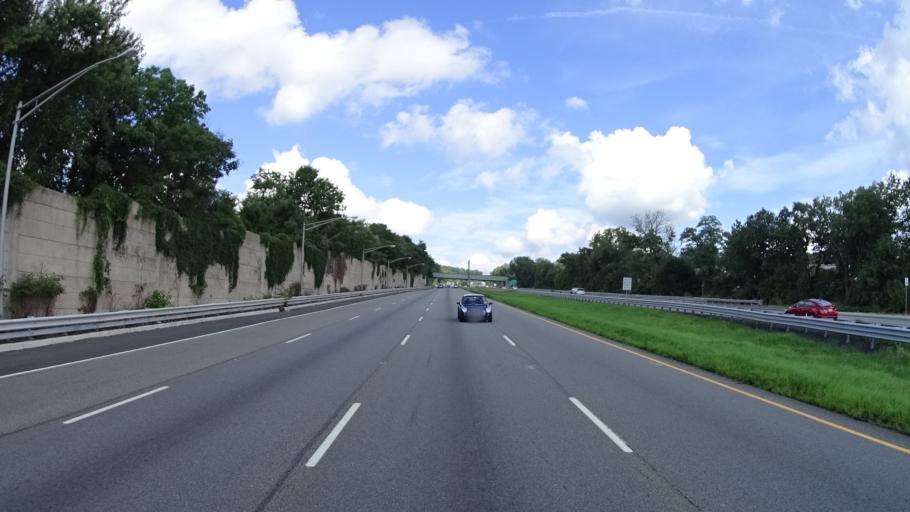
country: US
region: New Jersey
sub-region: Union County
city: Springfield
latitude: 40.7210
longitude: -74.3359
